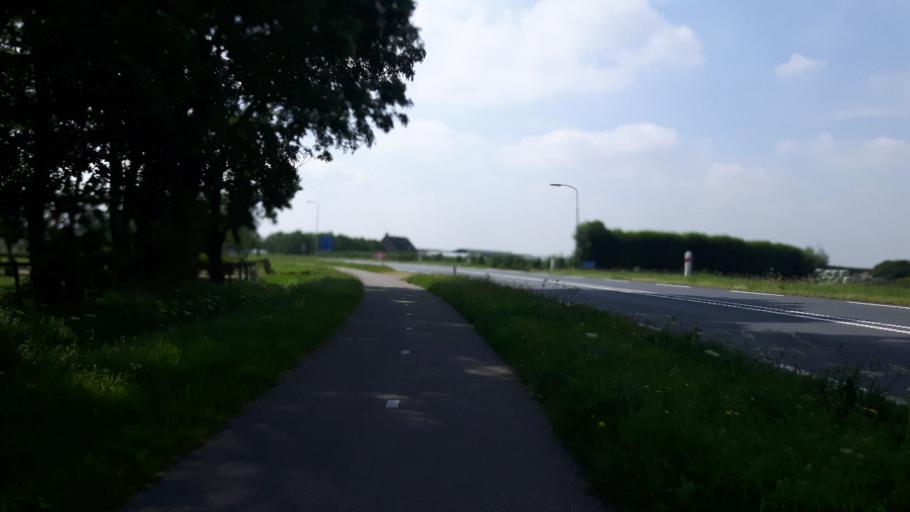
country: NL
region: Utrecht
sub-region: Gemeente Montfoort
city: Montfoort
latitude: 52.0487
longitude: 4.9278
